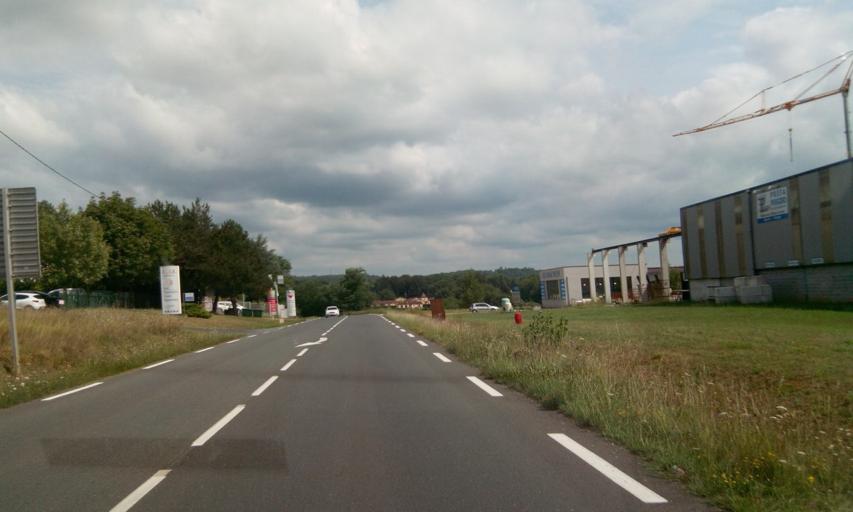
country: FR
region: Aquitaine
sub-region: Departement de la Dordogne
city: Carsac-Aillac
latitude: 44.8636
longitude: 1.2575
